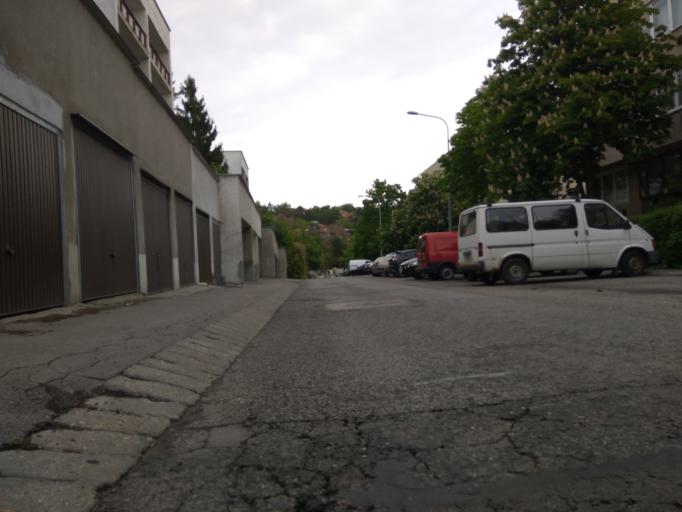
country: HU
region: Budapest
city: Budapest XII. keruelet
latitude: 47.4950
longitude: 18.9984
